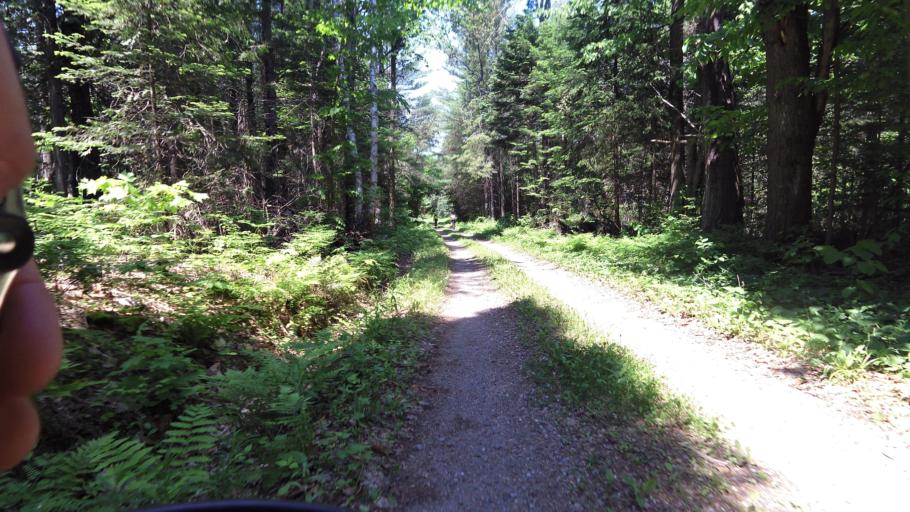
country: CA
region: Quebec
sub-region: Outaouais
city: Wakefield
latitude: 45.5838
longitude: -75.9555
